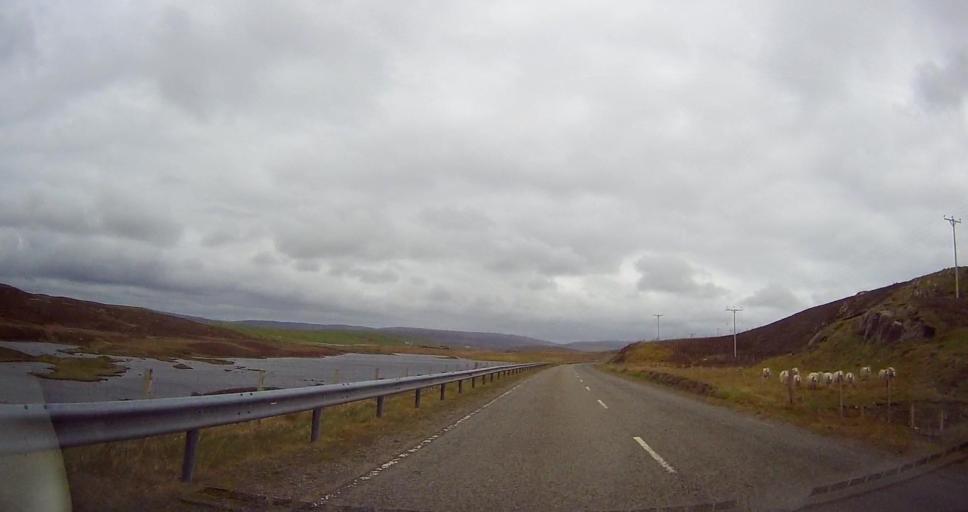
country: GB
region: Scotland
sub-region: Shetland Islands
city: Lerwick
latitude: 60.2578
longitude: -1.4757
